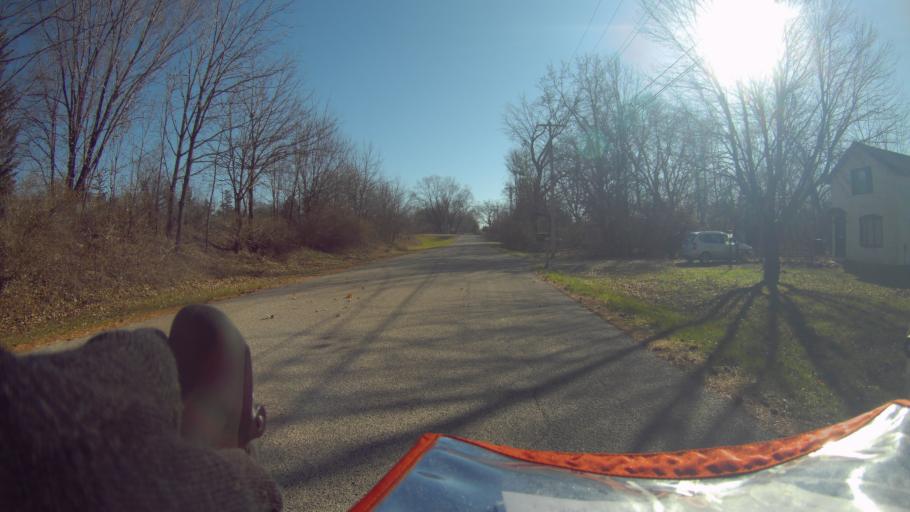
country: US
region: Wisconsin
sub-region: Green County
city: Brooklyn
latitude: 42.8512
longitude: -89.3700
